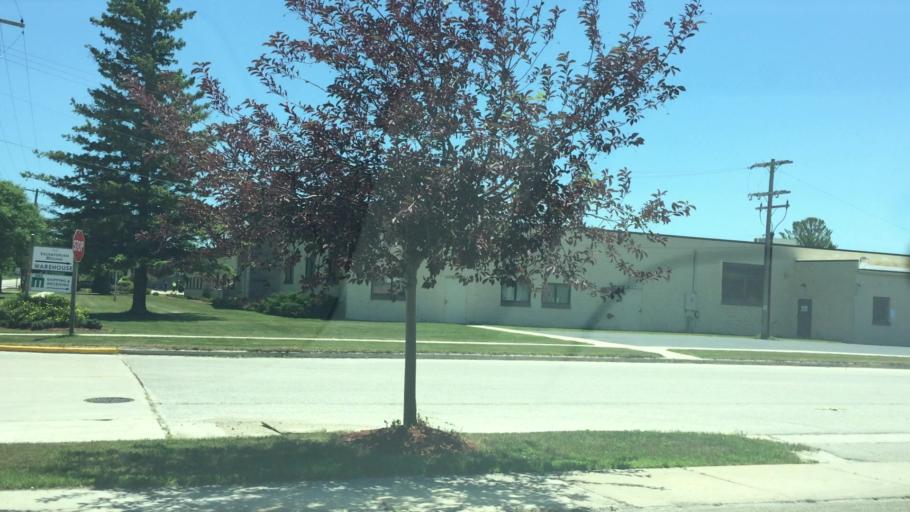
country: US
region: Wisconsin
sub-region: Calumet County
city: New Holstein
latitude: 43.9463
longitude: -88.0788
